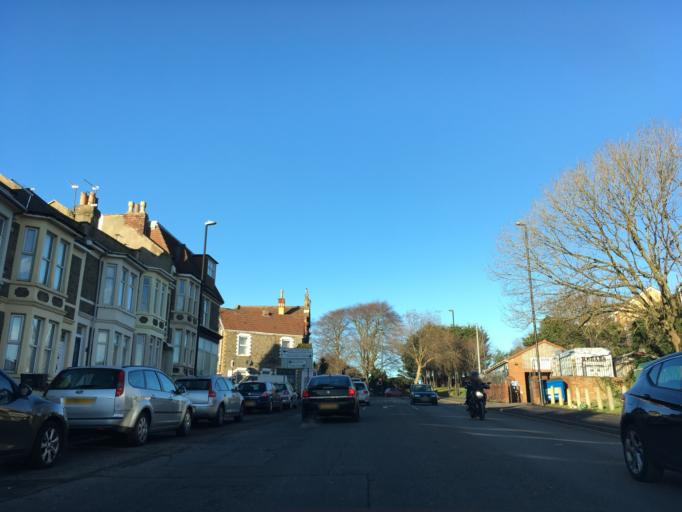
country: GB
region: England
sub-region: South Gloucestershire
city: Stoke Gifford
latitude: 51.4722
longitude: -2.5518
